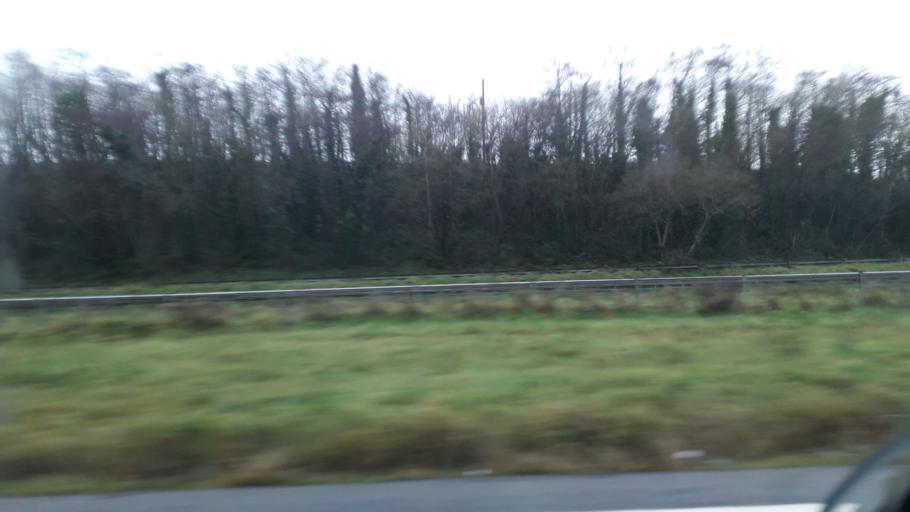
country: IE
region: Ulster
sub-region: County Donegal
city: Letterkenny
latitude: 54.9513
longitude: -7.6572
